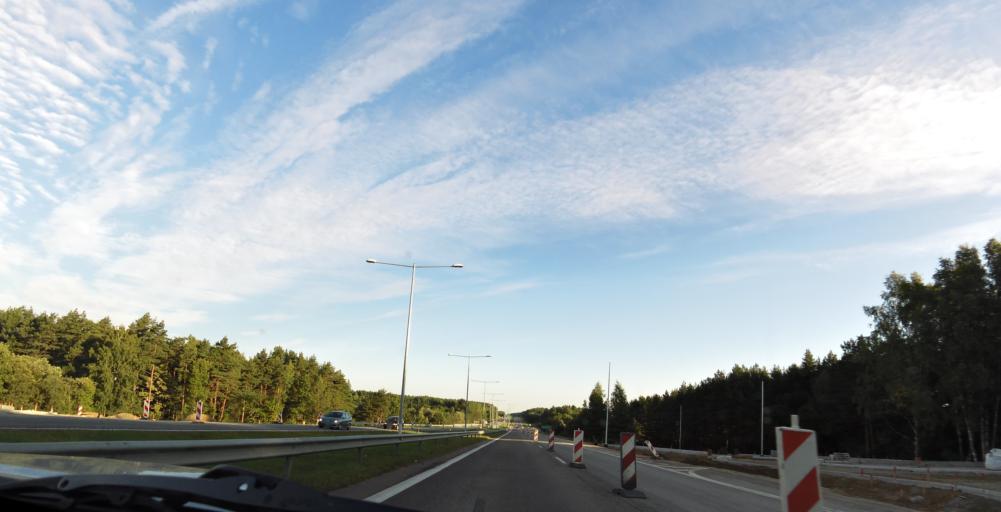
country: LT
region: Vilnius County
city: Ukmerge
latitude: 55.2519
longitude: 24.8175
